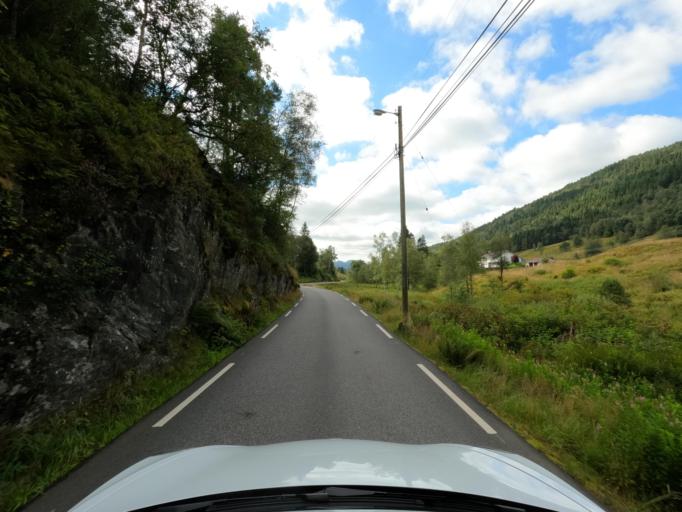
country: NO
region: Hordaland
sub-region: Os
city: Syfteland
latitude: 60.2938
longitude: 5.4824
